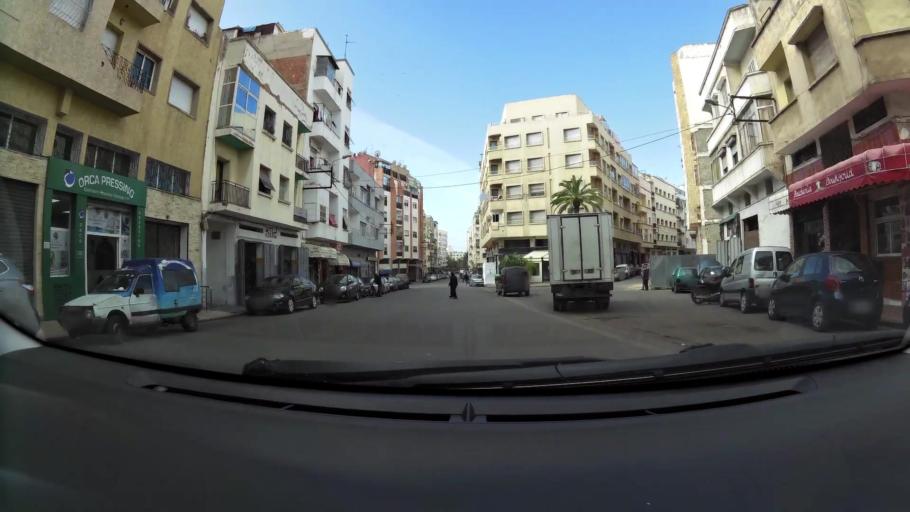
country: MA
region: Grand Casablanca
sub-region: Casablanca
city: Casablanca
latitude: 33.5942
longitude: -7.5903
